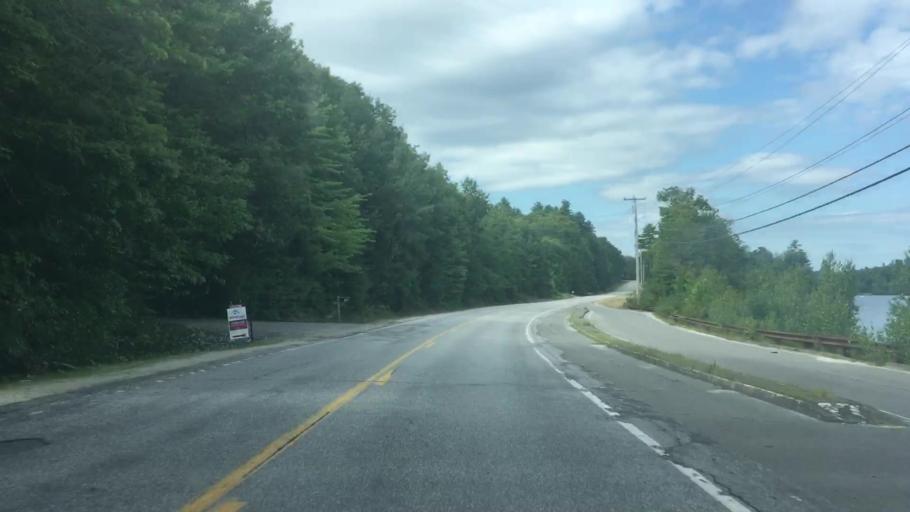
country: US
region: Maine
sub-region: Cumberland County
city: Raymond
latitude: 43.9945
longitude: -70.5183
